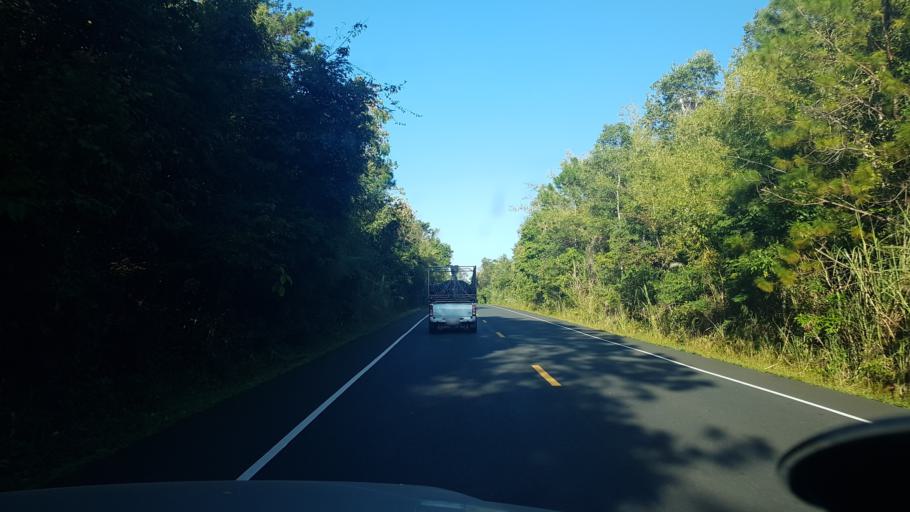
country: TH
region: Phetchabun
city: Nam Nao
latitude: 16.7020
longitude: 101.6127
